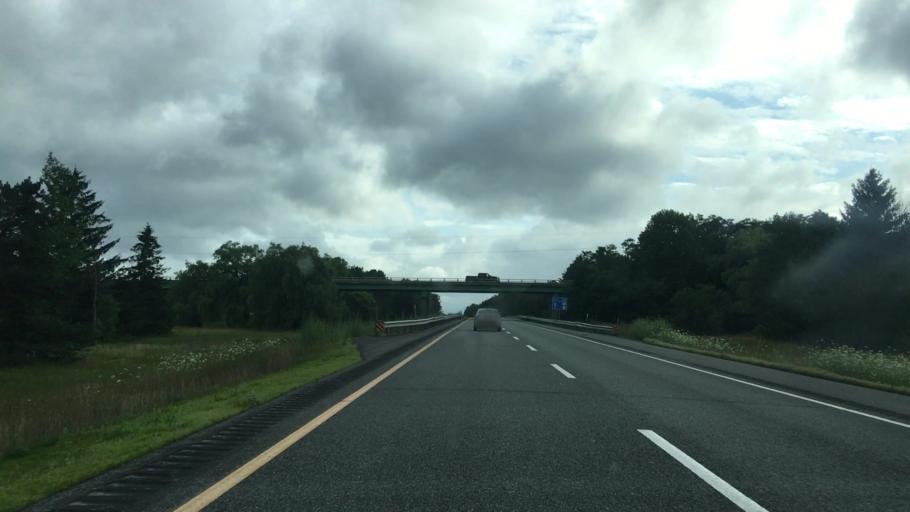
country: US
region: Maine
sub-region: Kennebec County
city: Clinton
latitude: 44.6513
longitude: -69.5146
